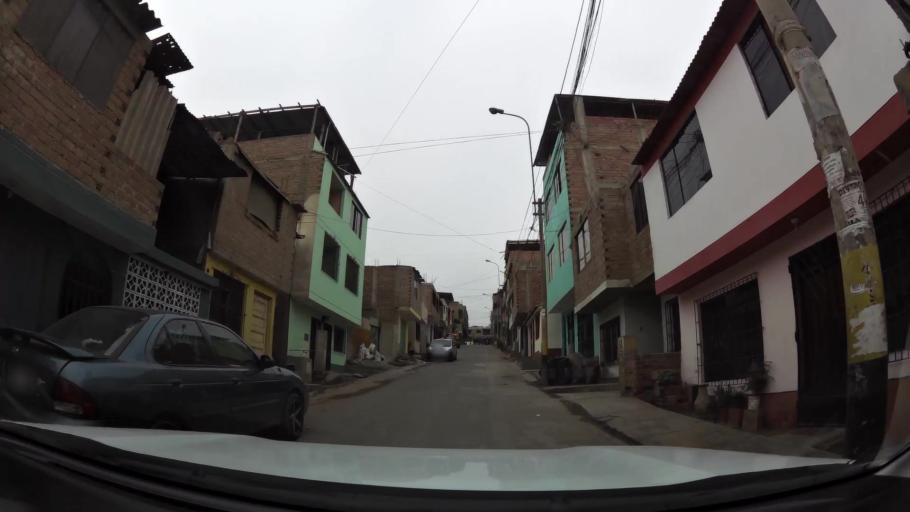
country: PE
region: Lima
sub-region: Lima
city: Surco
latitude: -12.1751
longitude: -76.9637
